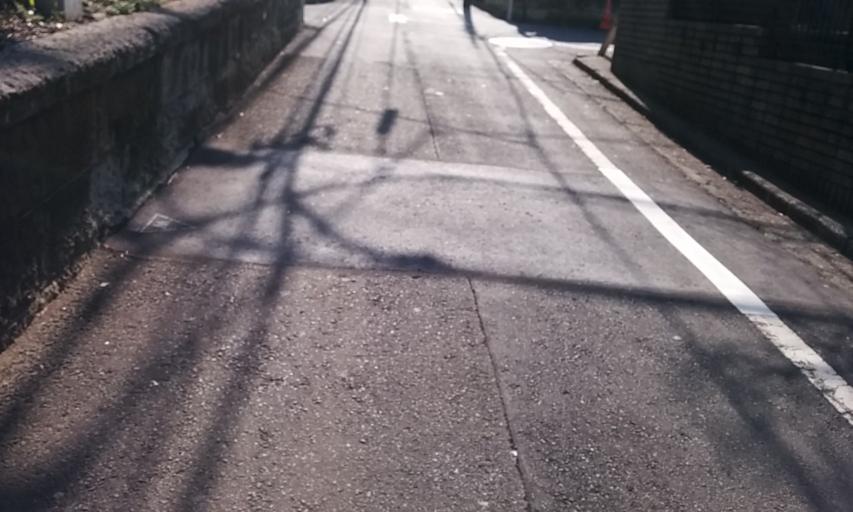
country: JP
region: Tokyo
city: Tokyo
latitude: 35.6650
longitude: 139.7076
